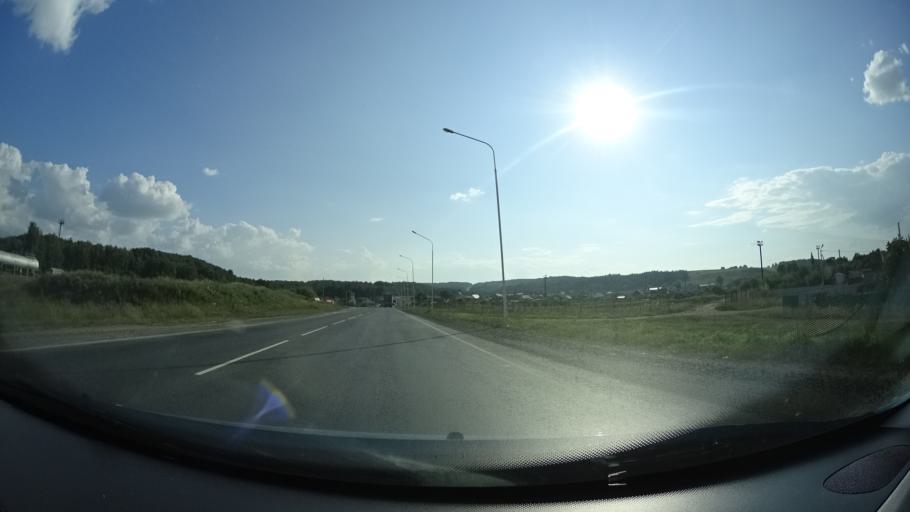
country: RU
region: Tatarstan
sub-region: Bavlinskiy Rayon
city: Bavly
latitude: 54.4611
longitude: 53.2851
